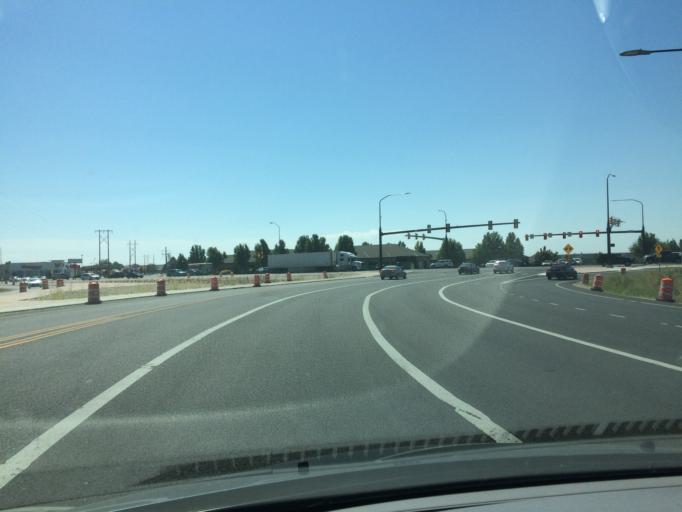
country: US
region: Utah
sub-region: Weber County
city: Uintah
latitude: 41.1564
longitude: -111.9399
